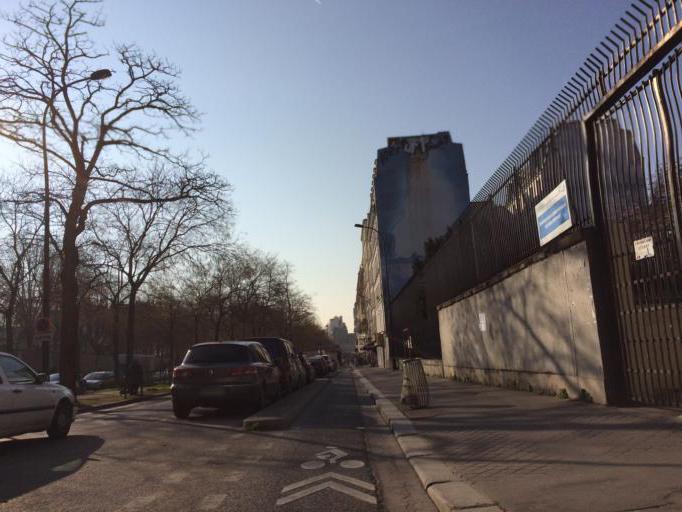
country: FR
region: Ile-de-France
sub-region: Departement de Seine-Saint-Denis
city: Le Pre-Saint-Gervais
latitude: 48.8617
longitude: 2.3878
